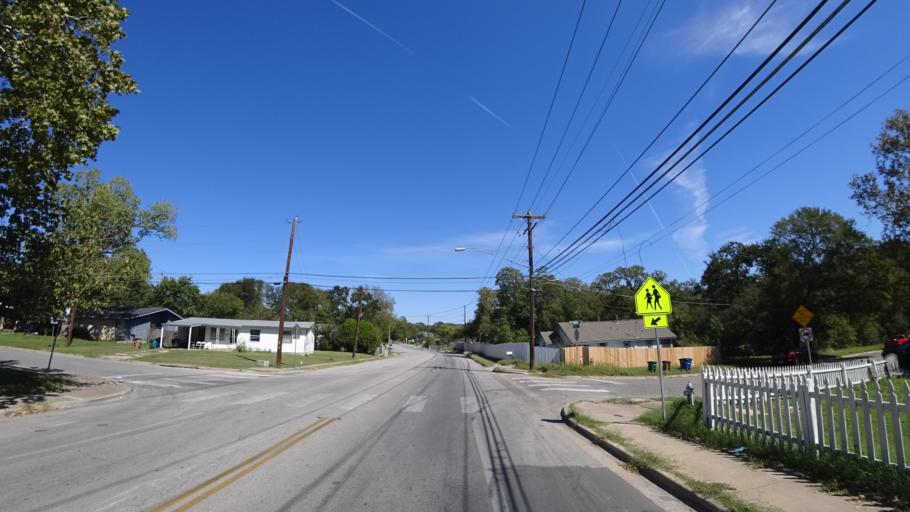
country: US
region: Texas
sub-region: Travis County
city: Austin
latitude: 30.2800
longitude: -97.6802
